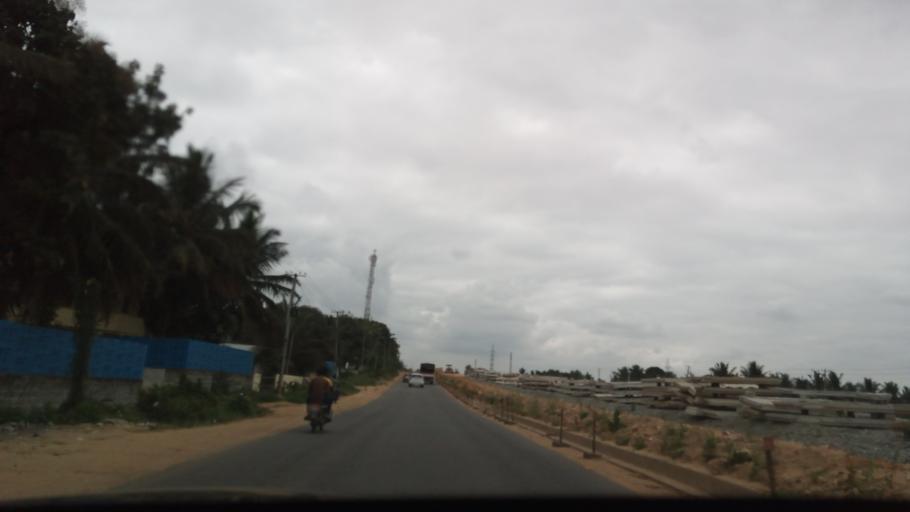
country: IN
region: Karnataka
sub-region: Mandya
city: Mandya
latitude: 12.4965
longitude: 76.8080
